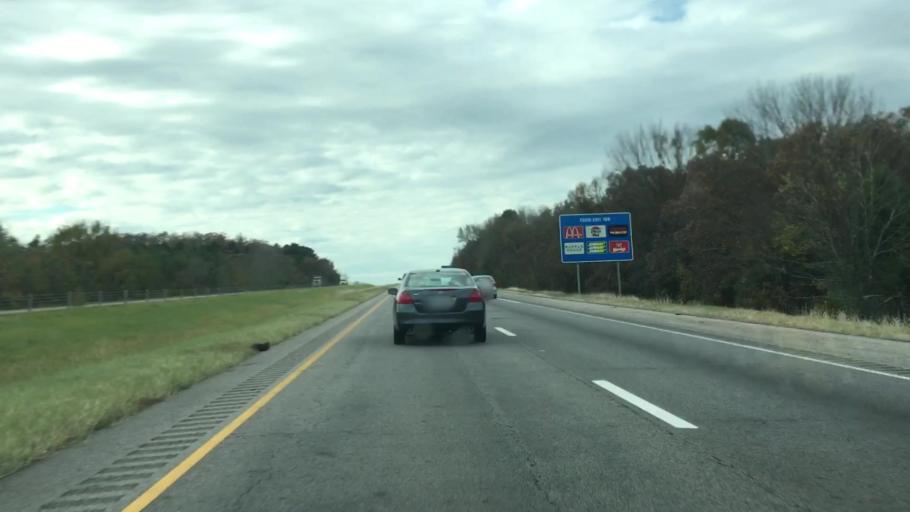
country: US
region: Arkansas
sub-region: Conway County
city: Morrilton
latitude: 35.1688
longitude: -92.6905
